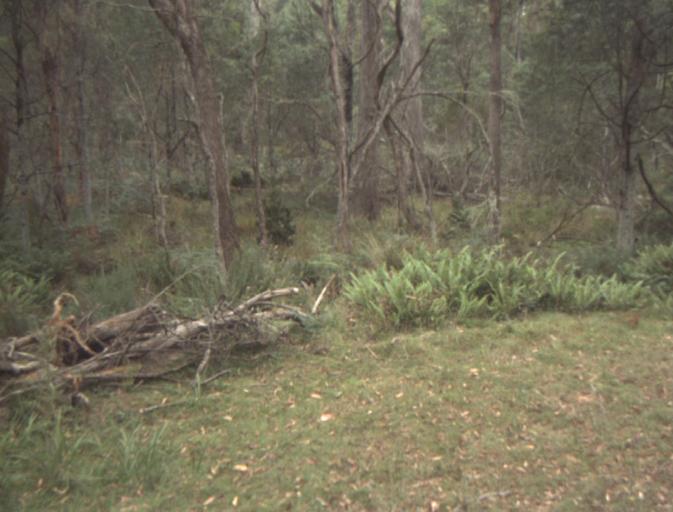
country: AU
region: Tasmania
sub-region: Dorset
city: Scottsdale
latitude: -41.4492
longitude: 147.5227
